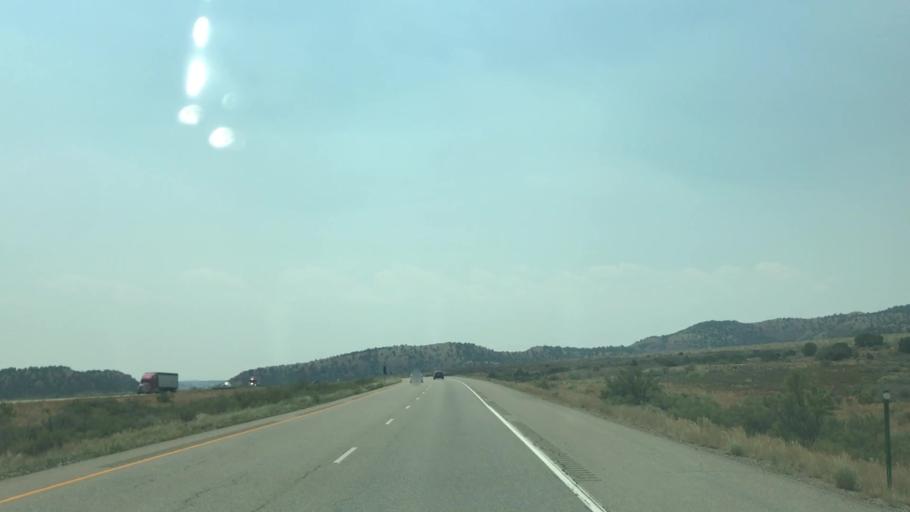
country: US
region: Colorado
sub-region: Garfield County
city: Parachute
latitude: 39.3856
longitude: -108.1469
